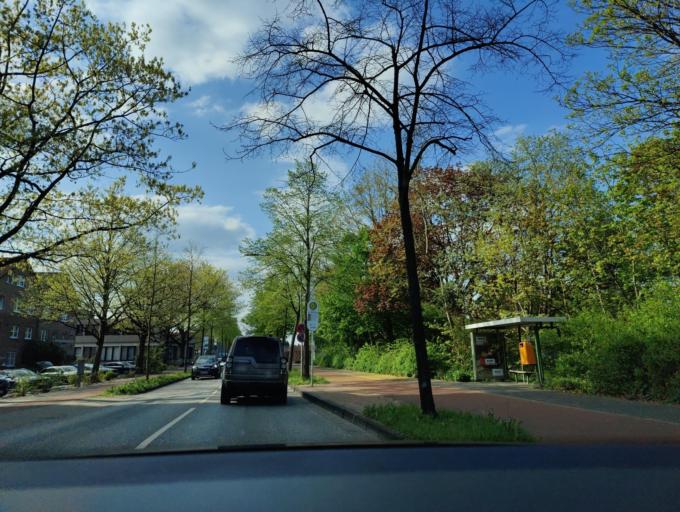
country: DE
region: Lower Saxony
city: Nordhorn
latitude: 52.4184
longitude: 7.0663
